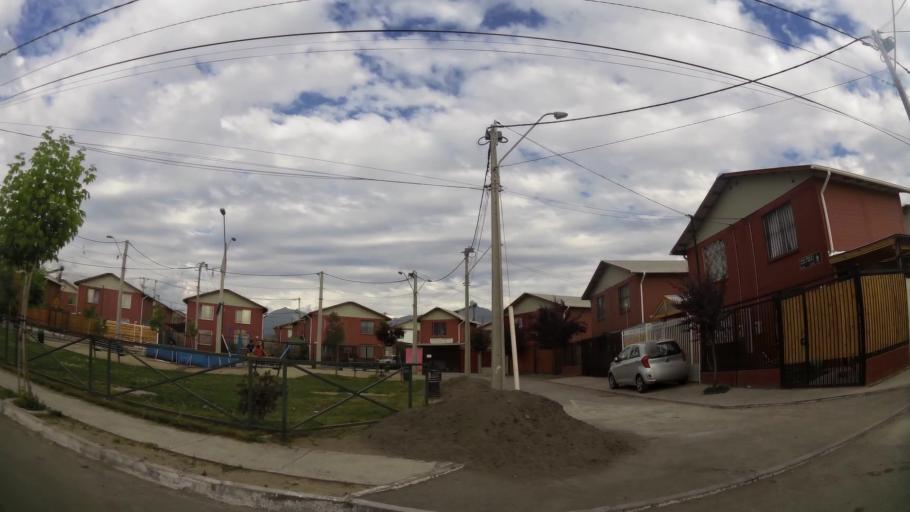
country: CL
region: Santiago Metropolitan
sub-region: Provincia de Cordillera
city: Puente Alto
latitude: -33.6291
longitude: -70.6024
